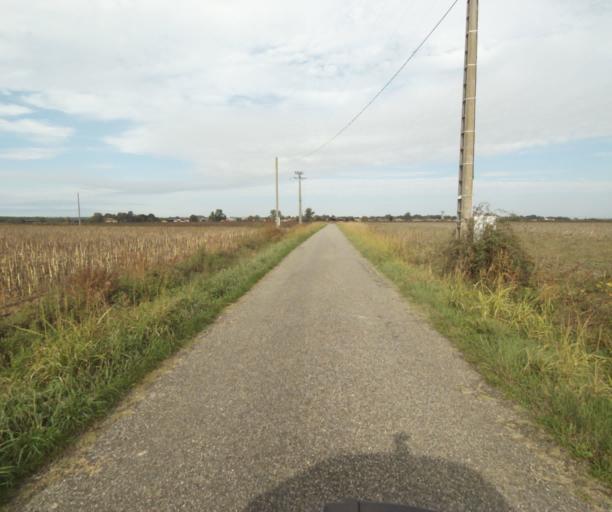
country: FR
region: Midi-Pyrenees
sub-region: Departement du Tarn-et-Garonne
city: Finhan
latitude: 43.9045
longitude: 1.2352
